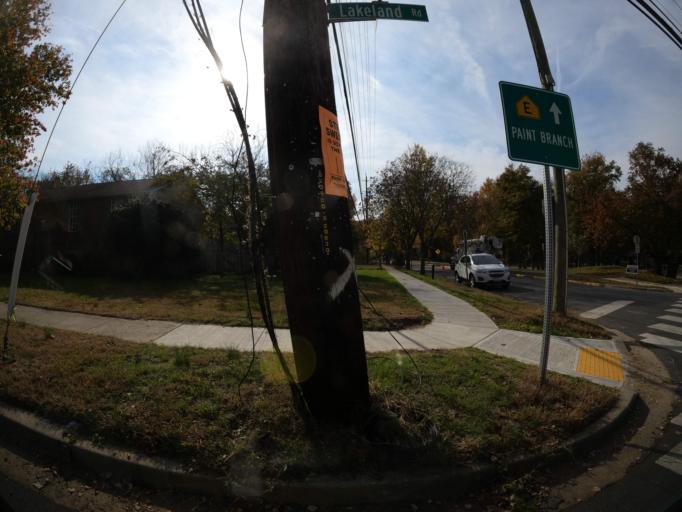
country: US
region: Maryland
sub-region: Prince George's County
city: College Park
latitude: 38.9889
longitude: -76.9287
